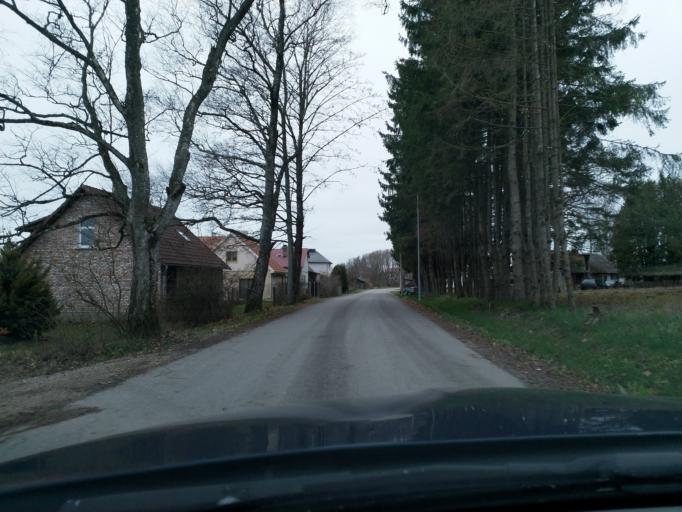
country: LV
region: Kuldigas Rajons
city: Kuldiga
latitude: 56.9700
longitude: 21.9985
